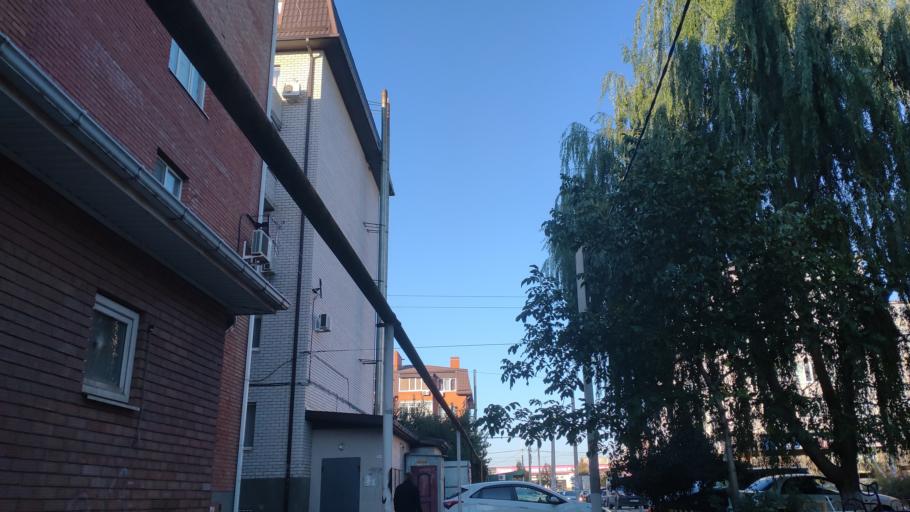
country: RU
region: Krasnodarskiy
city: Krasnodar
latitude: 45.0829
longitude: 39.0033
